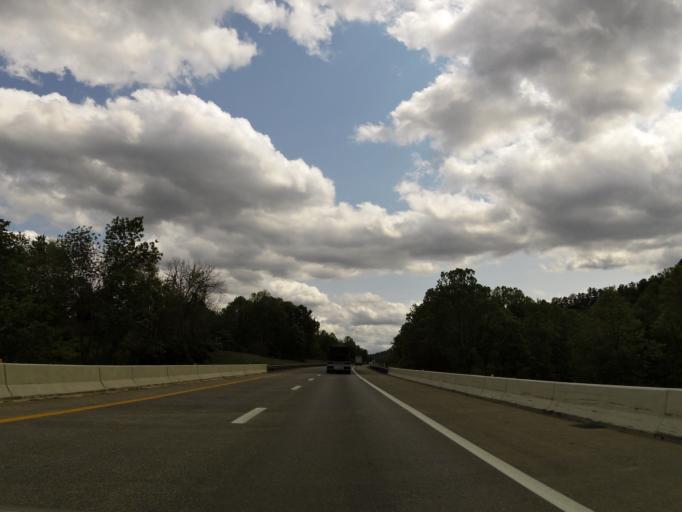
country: US
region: West Virginia
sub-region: Raleigh County
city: Bradley
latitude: 37.8947
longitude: -81.2671
